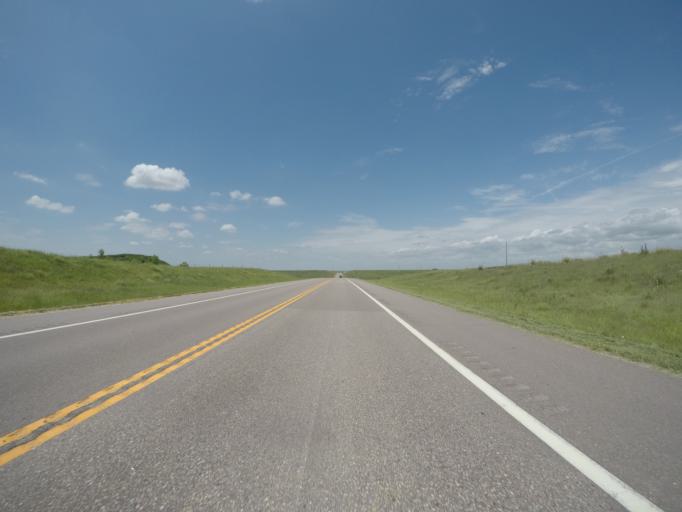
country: US
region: Kansas
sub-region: Graham County
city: Hill City
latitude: 39.3792
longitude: -99.7404
